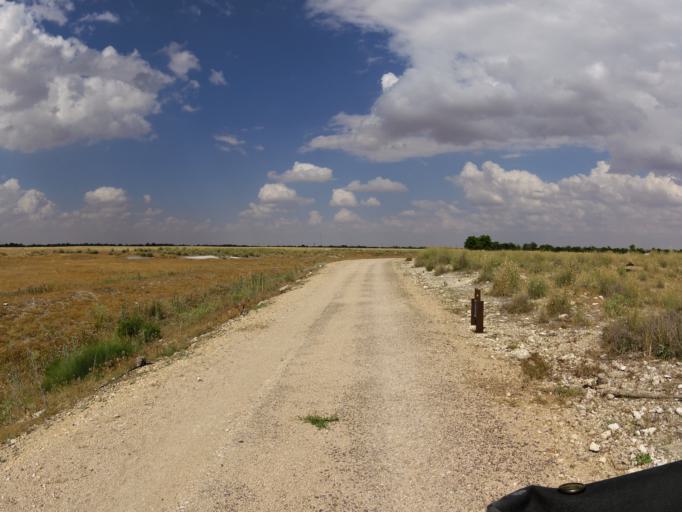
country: ES
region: Castille-La Mancha
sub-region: Provincia de Albacete
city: Albacete
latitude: 38.9656
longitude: -1.9520
